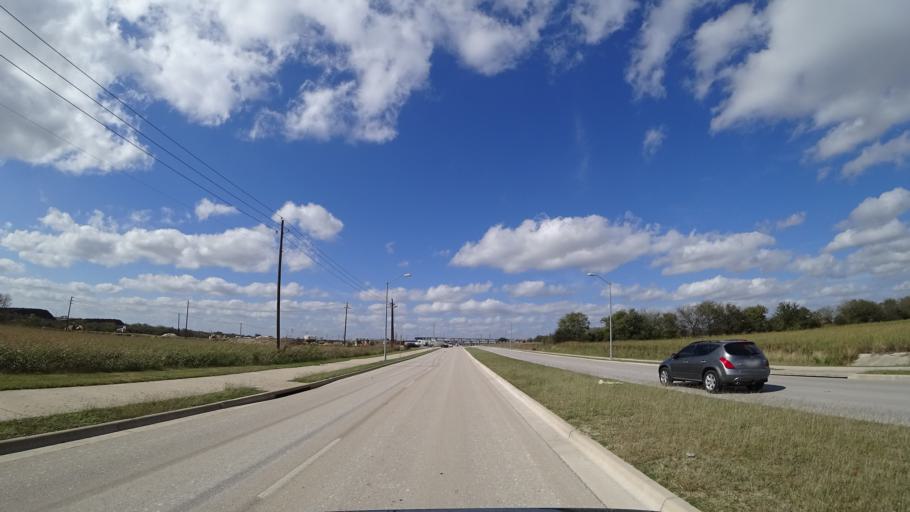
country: US
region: Texas
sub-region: Travis County
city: Windemere
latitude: 30.4757
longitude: -97.6603
